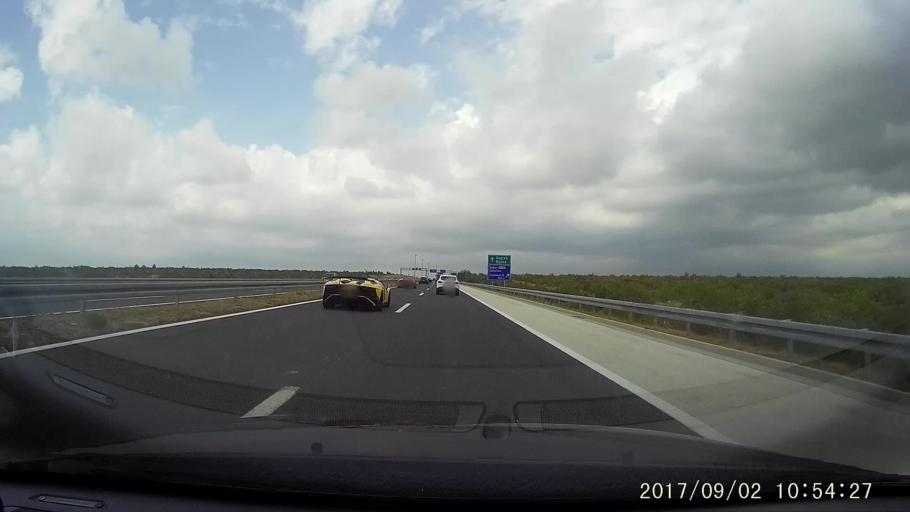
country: HR
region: Zadarska
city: Galovac
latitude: 44.1090
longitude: 15.4541
